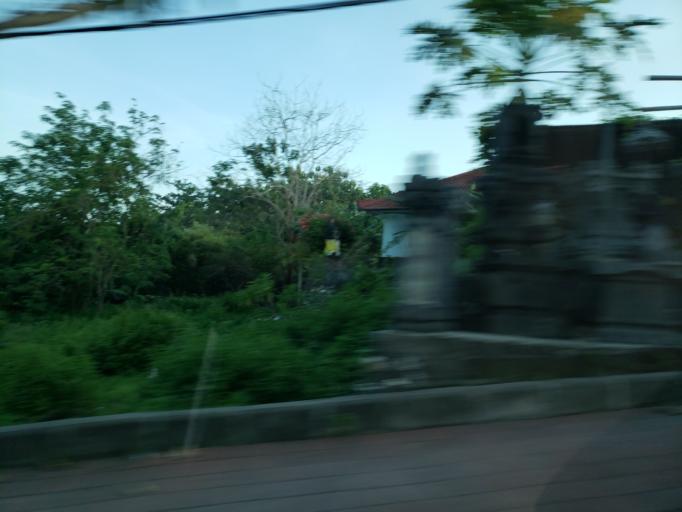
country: ID
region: Bali
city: Jimbaran
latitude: -8.7976
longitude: 115.1747
